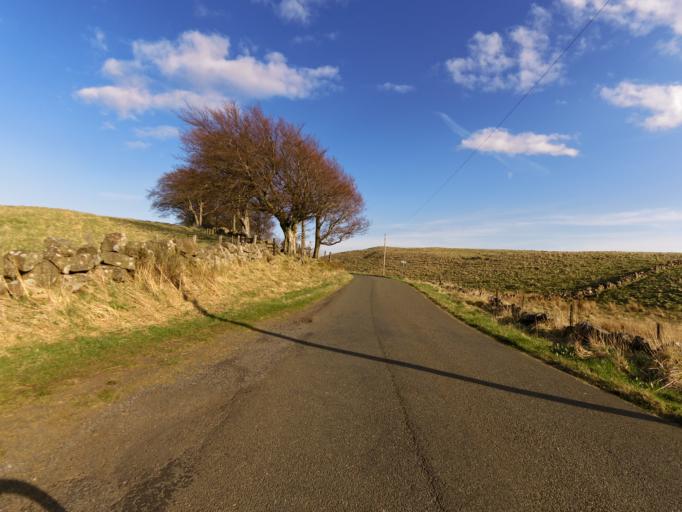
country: GB
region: Scotland
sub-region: Fife
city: Falkland
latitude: 56.2349
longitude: -3.2398
